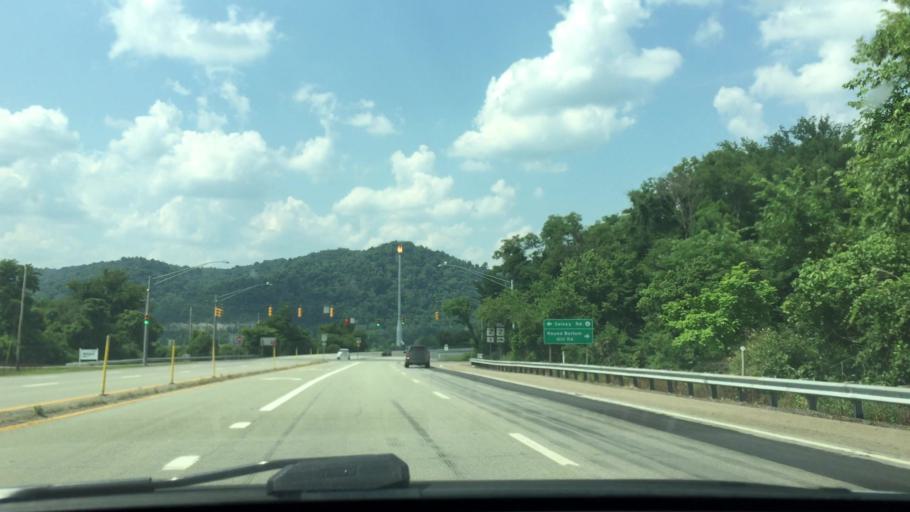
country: US
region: Ohio
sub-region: Belmont County
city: Powhatan Point
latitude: 39.9076
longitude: -80.7966
